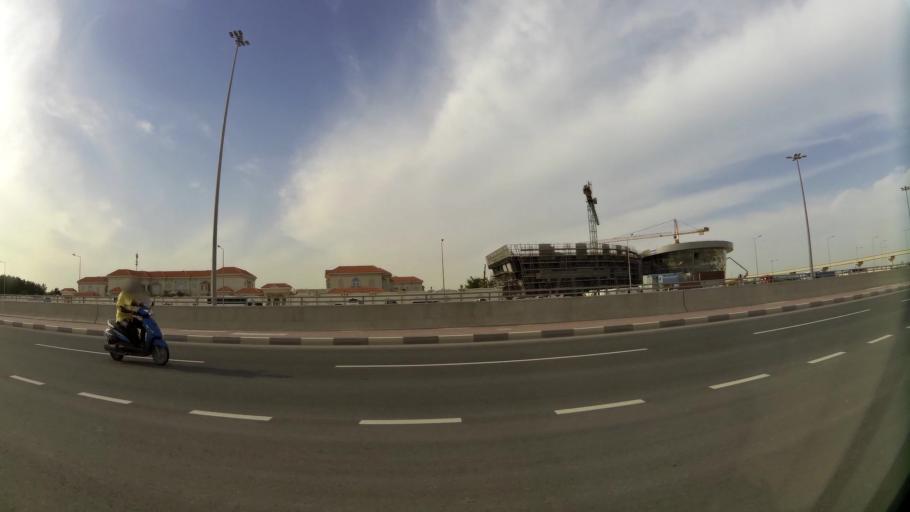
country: QA
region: Al Wakrah
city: Al Wakrah
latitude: 25.2305
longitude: 51.5745
